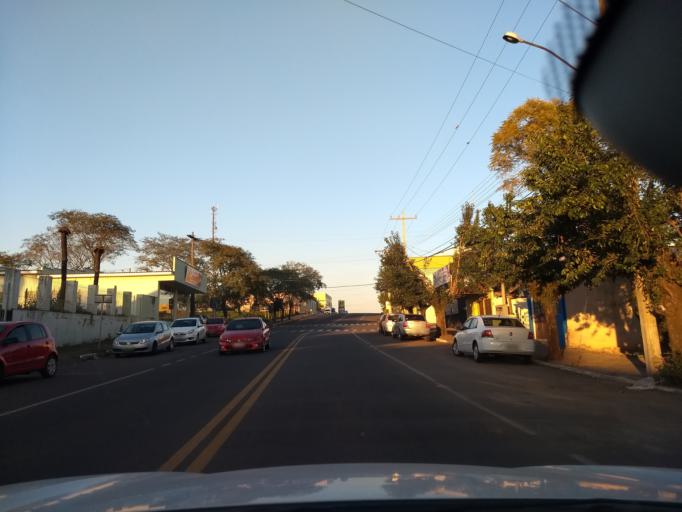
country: BR
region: Rio Grande do Sul
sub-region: Santa Cruz Do Sul
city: Santa Cruz do Sul
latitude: -29.7168
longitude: -52.5070
